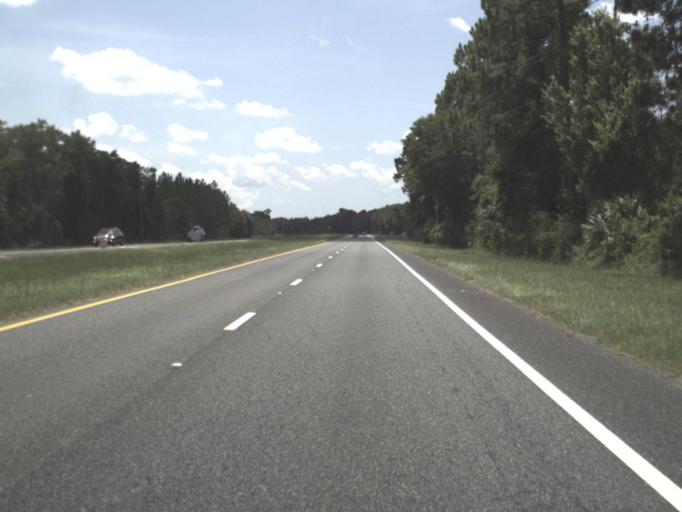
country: US
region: Florida
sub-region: Taylor County
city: Steinhatchee
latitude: 29.7548
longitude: -83.3221
